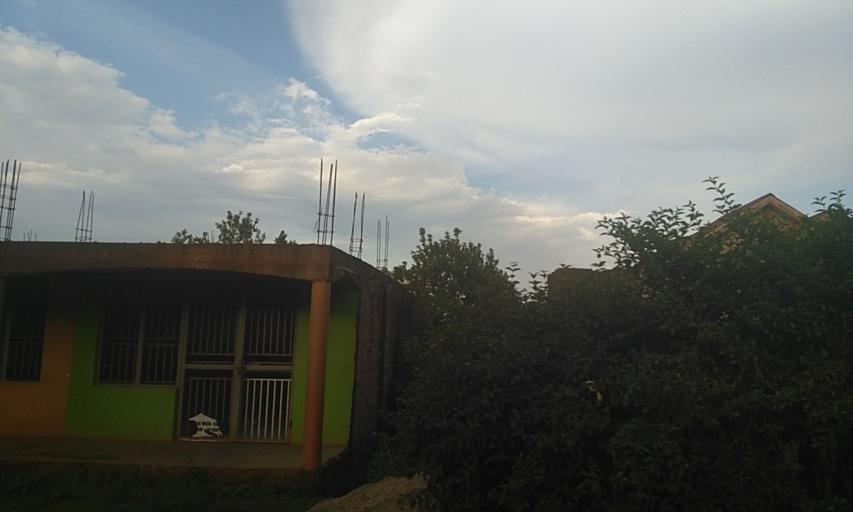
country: UG
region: Central Region
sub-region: Wakiso District
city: Kajansi
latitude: 0.2546
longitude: 32.5343
